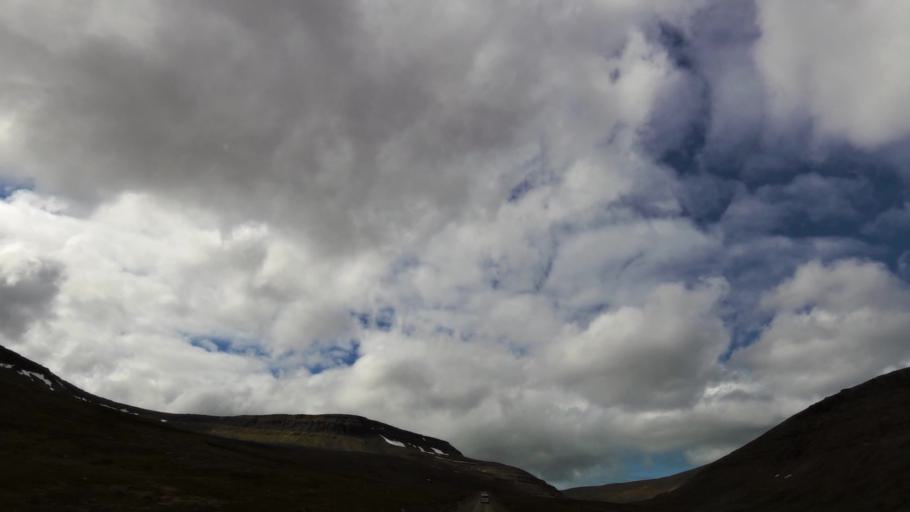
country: IS
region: Westfjords
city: Isafjoerdur
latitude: 66.1621
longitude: -23.3120
